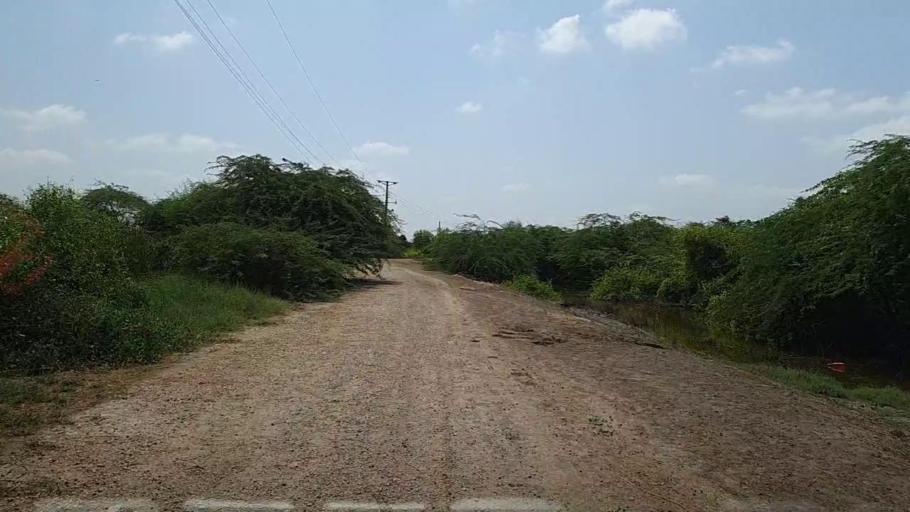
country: PK
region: Sindh
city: Kario
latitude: 24.6968
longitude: 68.6380
